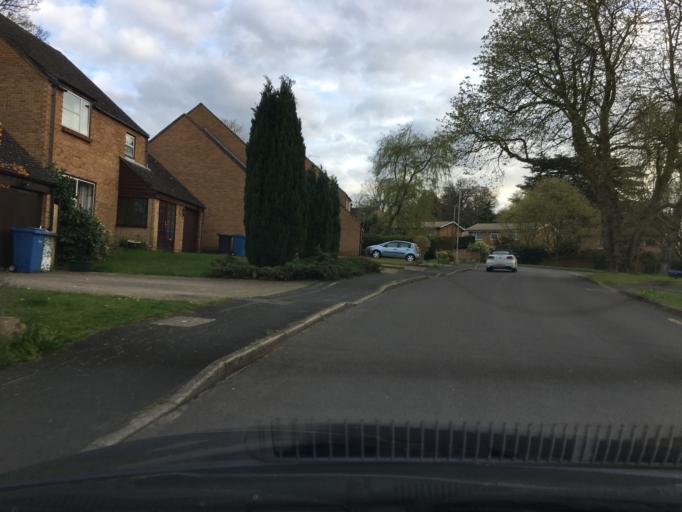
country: GB
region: England
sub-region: Hampshire
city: Yateley
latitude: 51.3370
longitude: -0.8175
